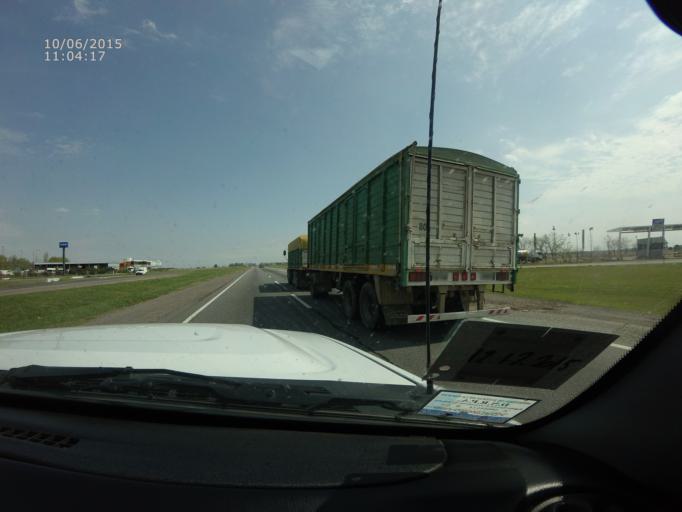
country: AR
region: Santa Fe
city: Arroyo Seco
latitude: -33.2273
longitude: -60.4601
